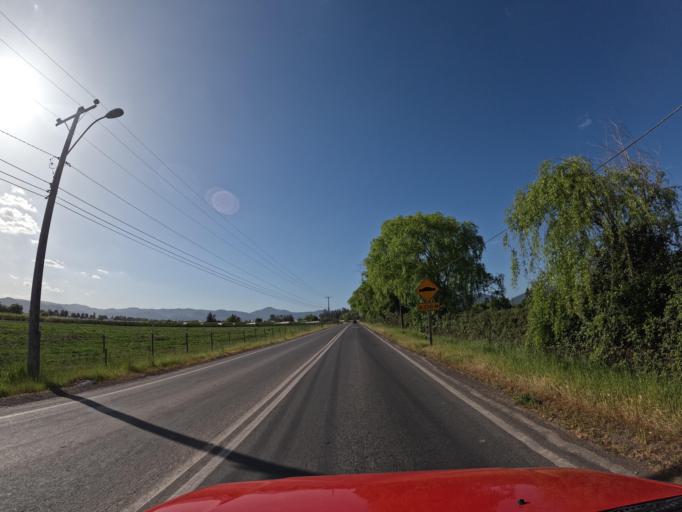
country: CL
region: Maule
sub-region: Provincia de Curico
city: Rauco
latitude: -34.8924
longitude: -71.2738
